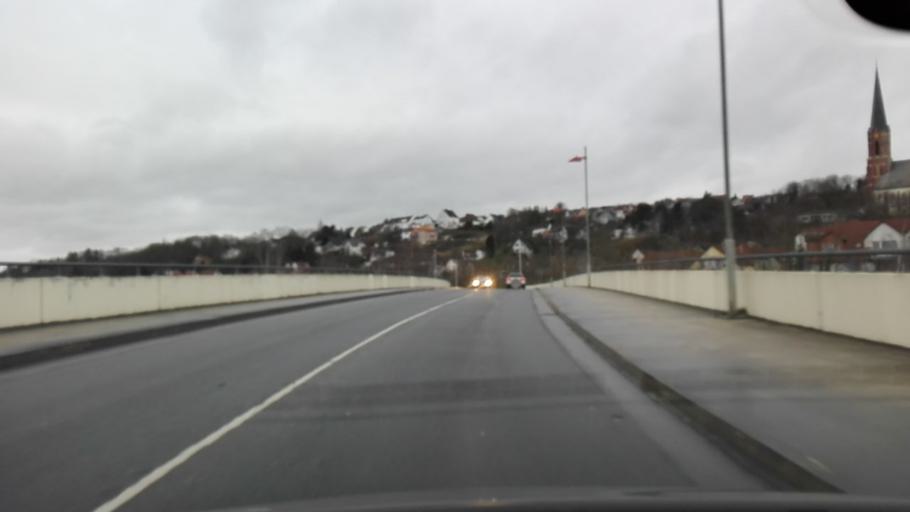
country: DE
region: North Rhine-Westphalia
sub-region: Regierungsbezirk Arnsberg
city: Frondenberg
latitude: 51.4709
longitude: 7.7653
